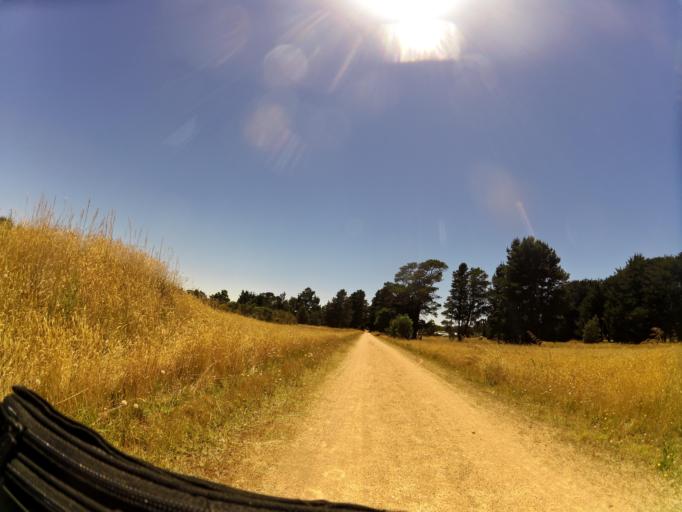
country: AU
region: Victoria
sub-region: Ballarat North
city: Delacombe
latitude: -37.6546
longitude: 143.6739
